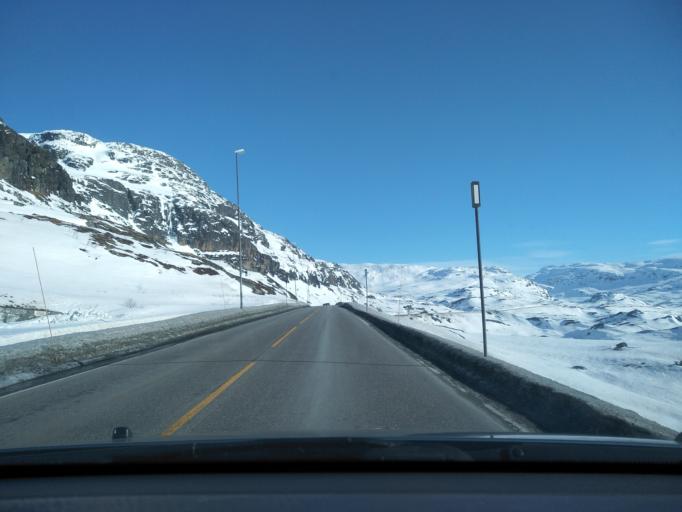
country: NO
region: Hordaland
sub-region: Odda
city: Odda
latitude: 59.8491
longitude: 6.9533
